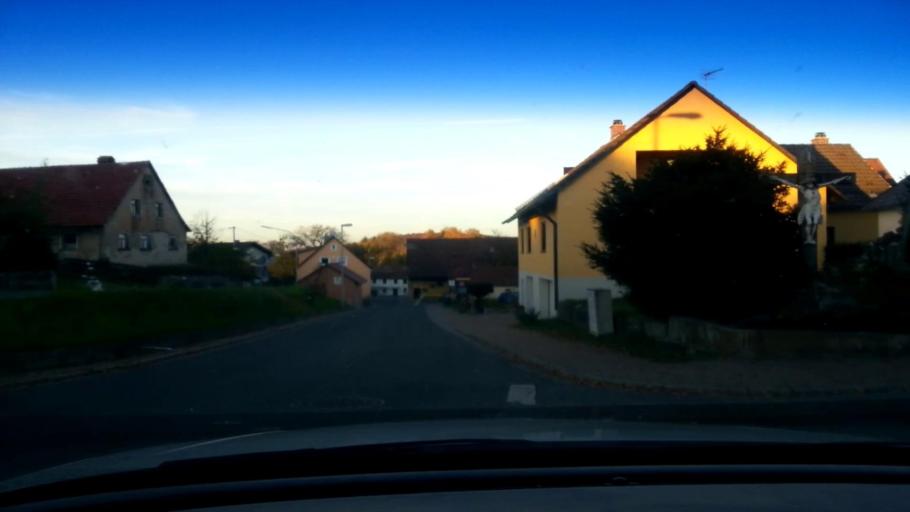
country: DE
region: Bavaria
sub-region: Upper Franconia
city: Heiligenstadt
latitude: 49.8462
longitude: 11.1192
